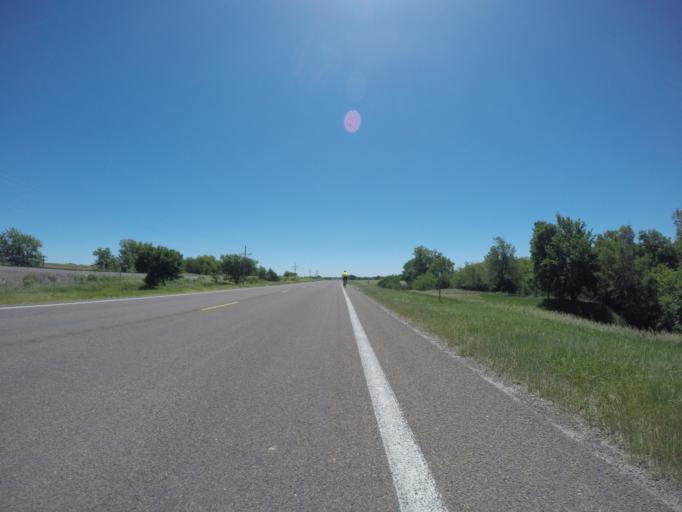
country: US
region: Kansas
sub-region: Phillips County
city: Phillipsburg
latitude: 39.8254
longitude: -99.5651
